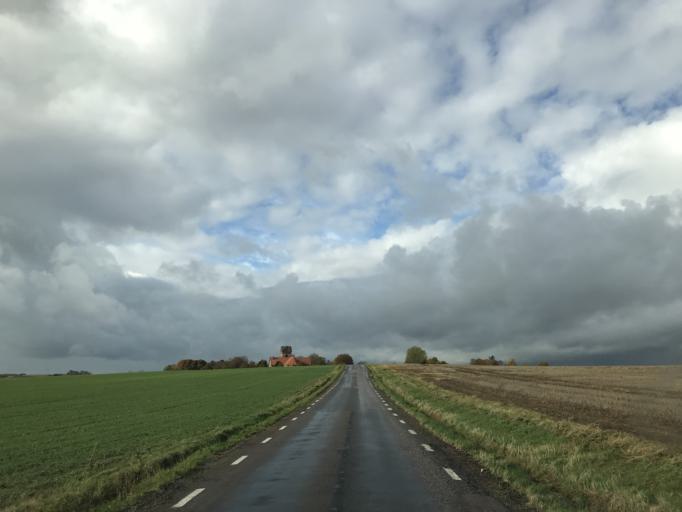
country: SE
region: Skane
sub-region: Svalovs Kommun
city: Svaloev
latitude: 55.9093
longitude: 13.1506
